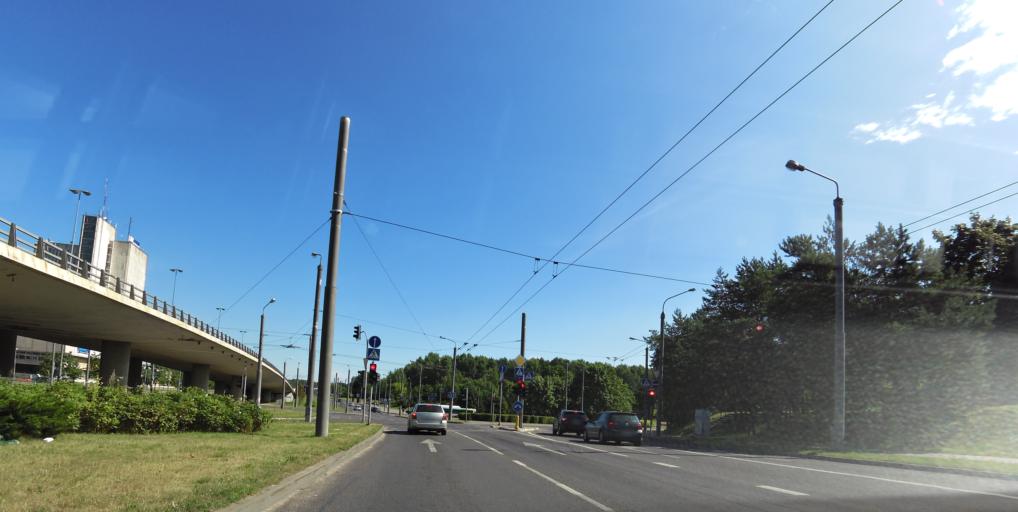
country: LT
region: Vilnius County
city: Justiniskes
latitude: 54.6986
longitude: 25.2221
